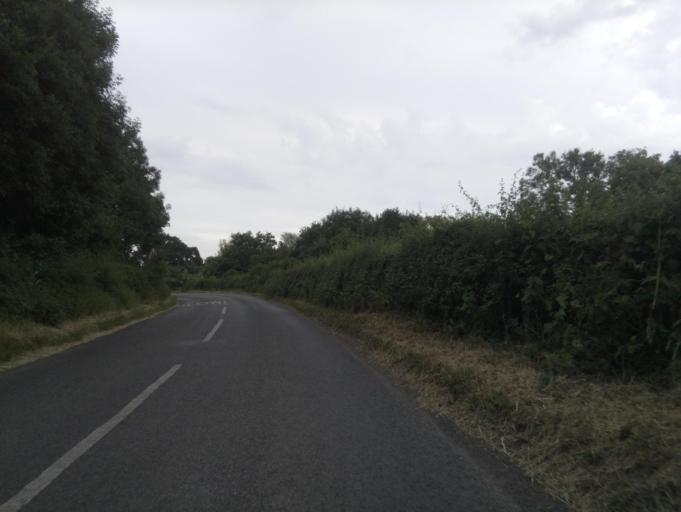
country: GB
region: England
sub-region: Somerset
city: Yeovil
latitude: 50.9156
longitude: -2.5855
